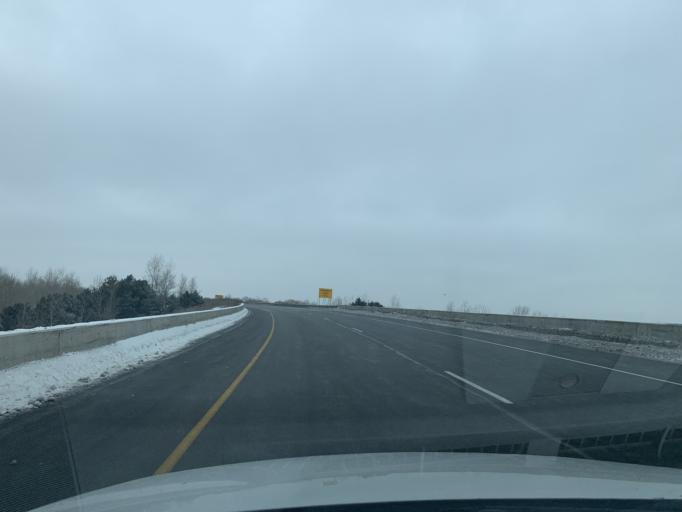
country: US
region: Minnesota
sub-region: Anoka County
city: Coon Rapids
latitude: 45.1228
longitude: -93.3063
